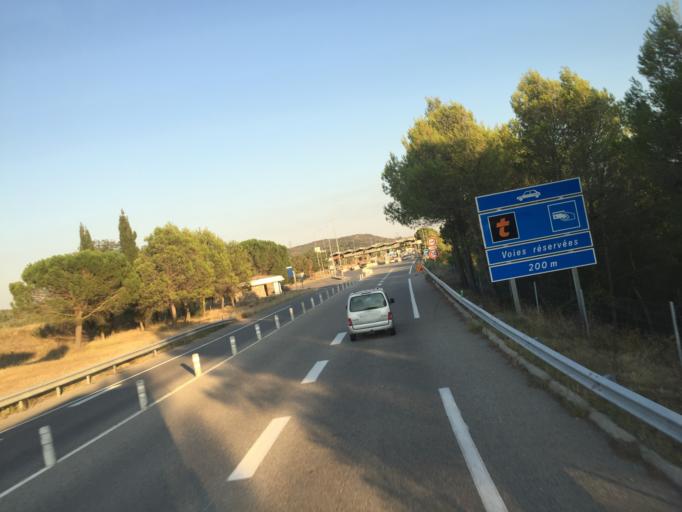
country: FR
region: Provence-Alpes-Cote d'Azur
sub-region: Departement du Vaucluse
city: Beaumont-de-Pertuis
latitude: 43.7036
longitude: 5.7321
